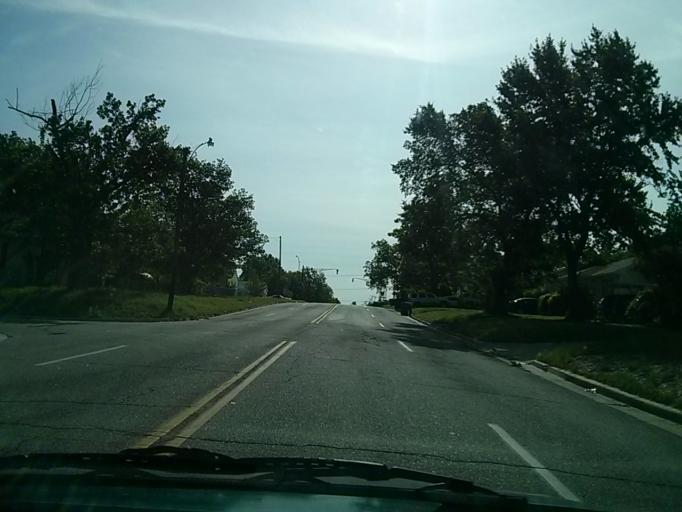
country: US
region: Oklahoma
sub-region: Tulsa County
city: Tulsa
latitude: 36.1552
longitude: -95.8972
